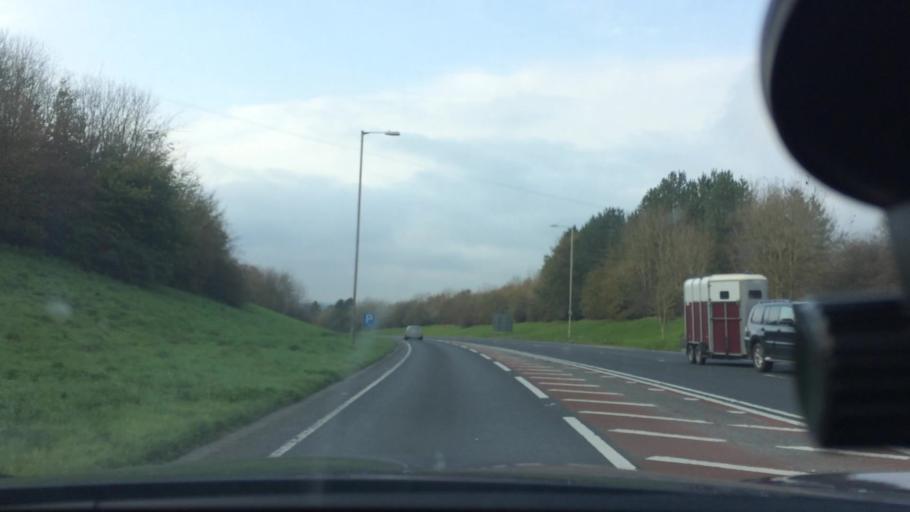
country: GB
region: England
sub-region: Devon
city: Axminster
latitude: 50.7664
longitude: -2.9790
